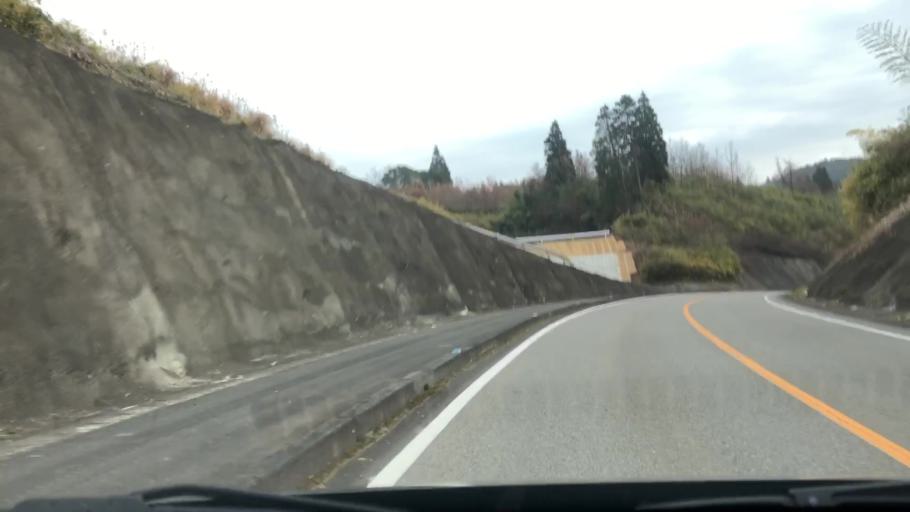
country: JP
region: Oita
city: Usuki
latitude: 33.0086
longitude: 131.6448
